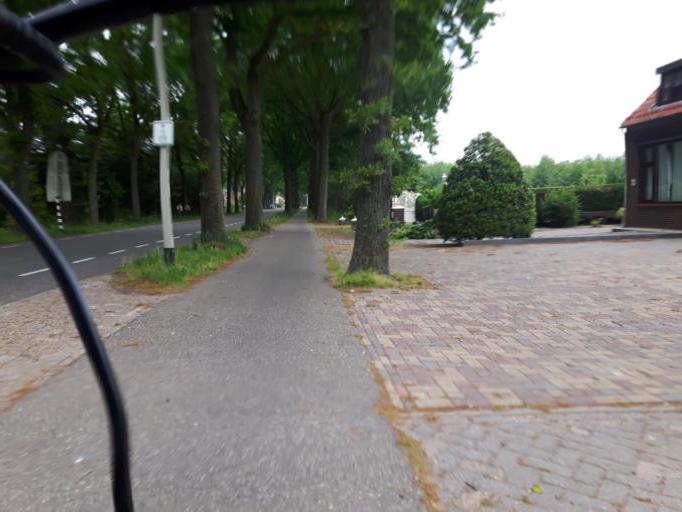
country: NL
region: North Brabant
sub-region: Gemeente Bergen op Zoom
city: Lepelstraat
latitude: 51.5453
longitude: 4.2871
